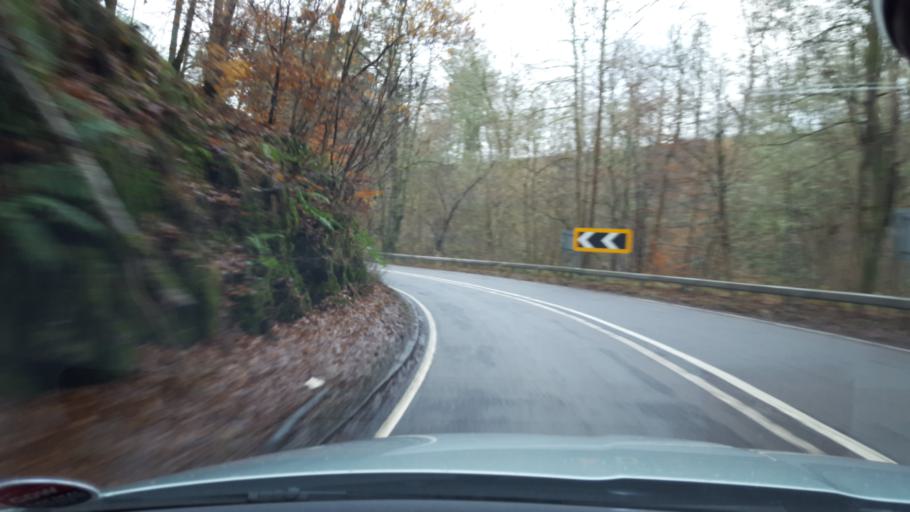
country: GB
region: Scotland
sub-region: Perth and Kinross
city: Bridge of Earn
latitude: 56.3029
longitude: -3.3686
